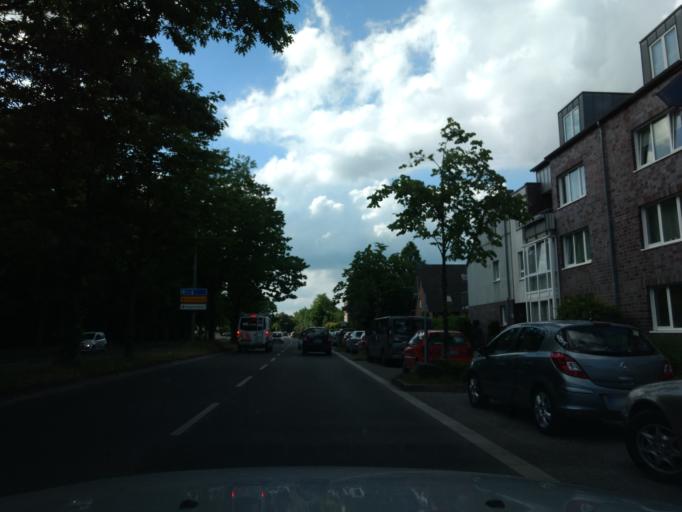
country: DE
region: North Rhine-Westphalia
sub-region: Regierungsbezirk Dusseldorf
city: Neuss
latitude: 51.1955
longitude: 6.6682
